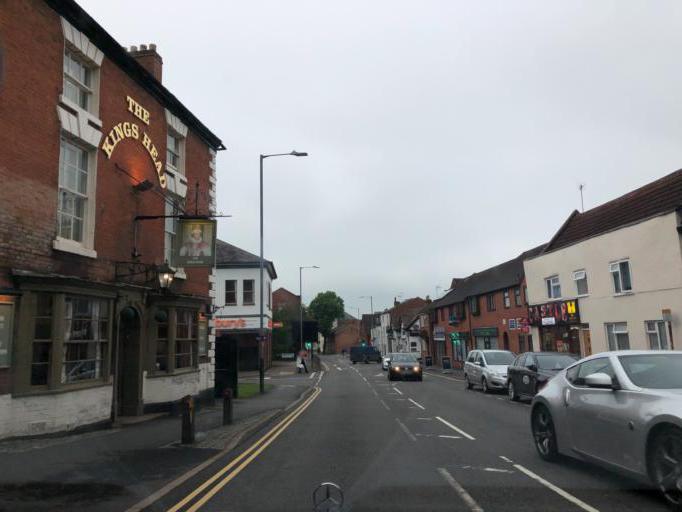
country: GB
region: England
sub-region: Warwickshire
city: Warwick
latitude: 52.2841
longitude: -1.5917
